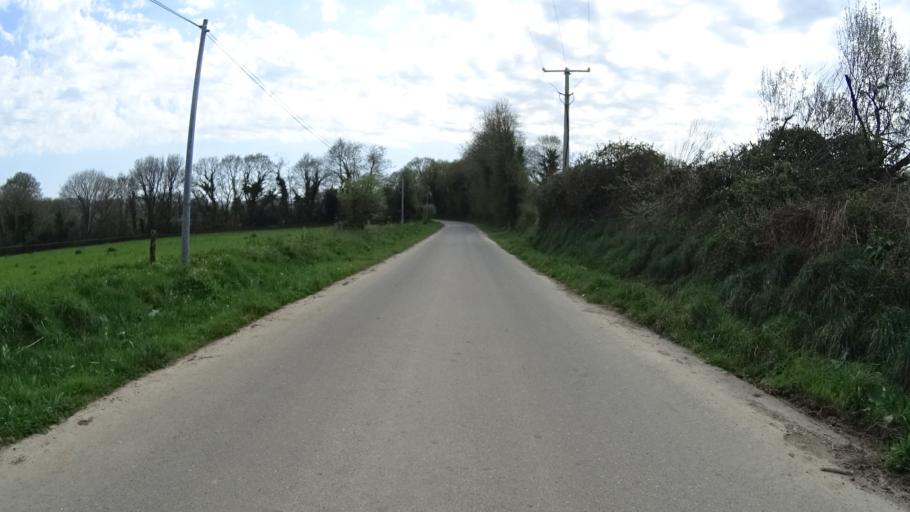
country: FR
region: Brittany
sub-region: Departement du Finistere
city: Sizun
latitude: 48.4189
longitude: -4.0569
